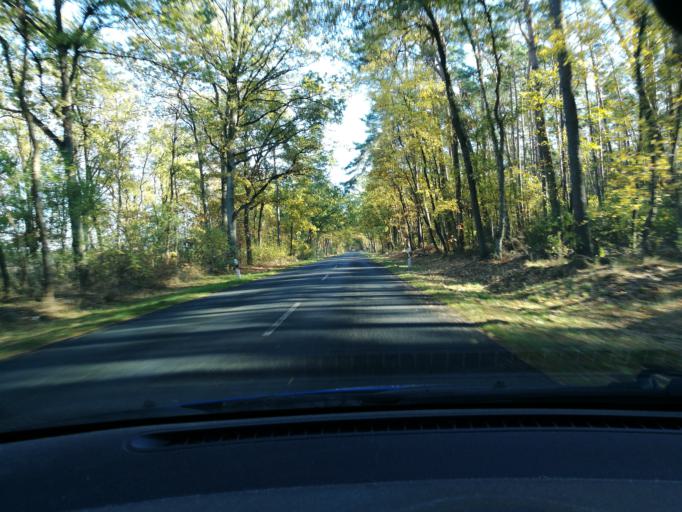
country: DE
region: Mecklenburg-Vorpommern
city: Neu Kaliss
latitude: 53.1273
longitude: 11.3283
